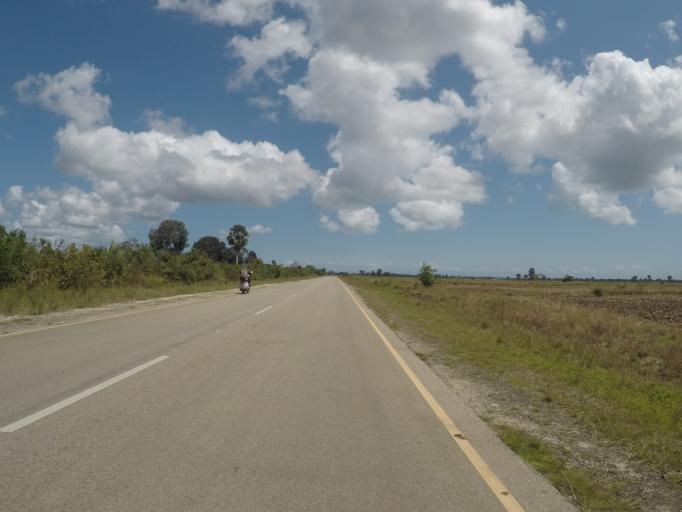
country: TZ
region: Zanzibar Central/South
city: Koani
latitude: -6.2028
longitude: 39.3684
